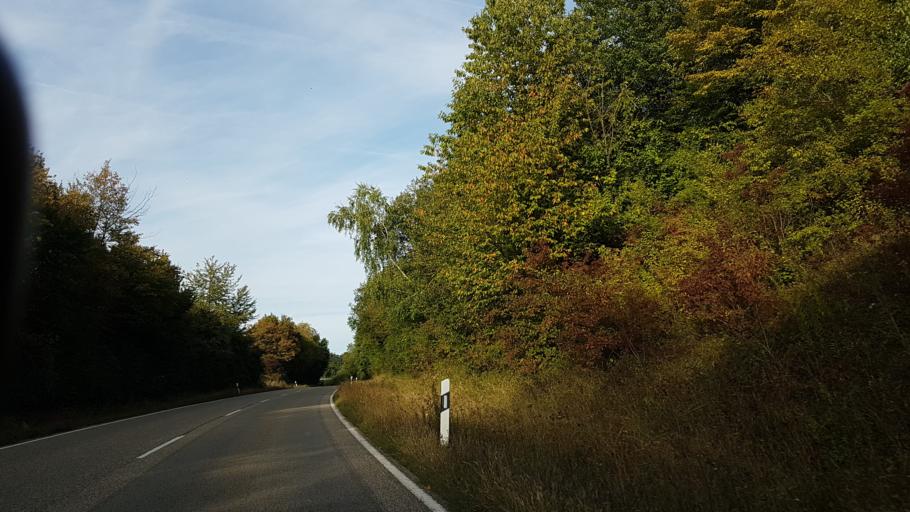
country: DE
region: Baden-Wuerttemberg
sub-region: Regierungsbezirk Stuttgart
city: Eberstadt
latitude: 49.1827
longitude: 9.3370
